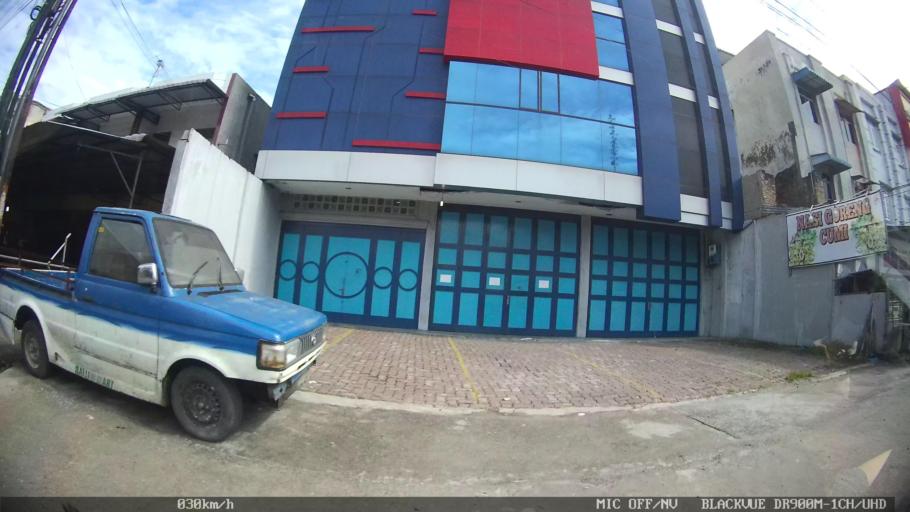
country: ID
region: North Sumatra
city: Medan
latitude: 3.6102
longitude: 98.6435
